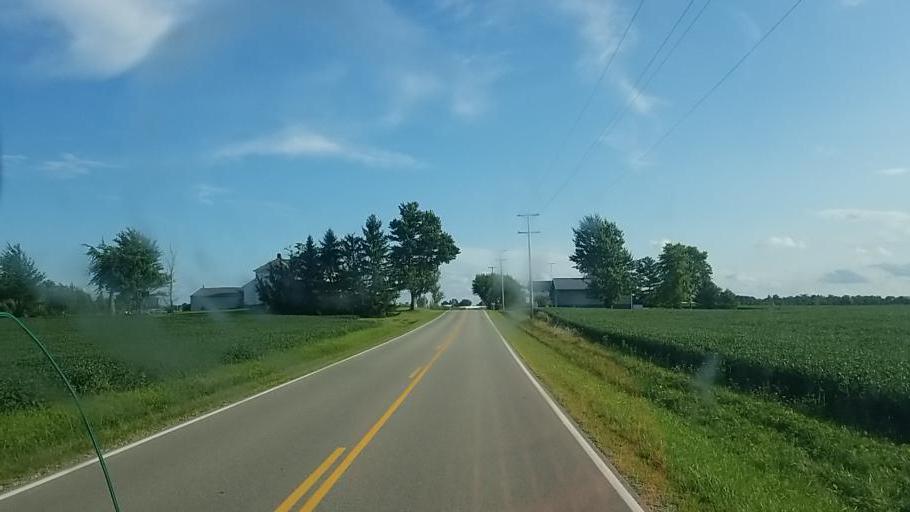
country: US
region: Ohio
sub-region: Crawford County
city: Bucyrus
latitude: 40.8253
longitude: -83.0931
